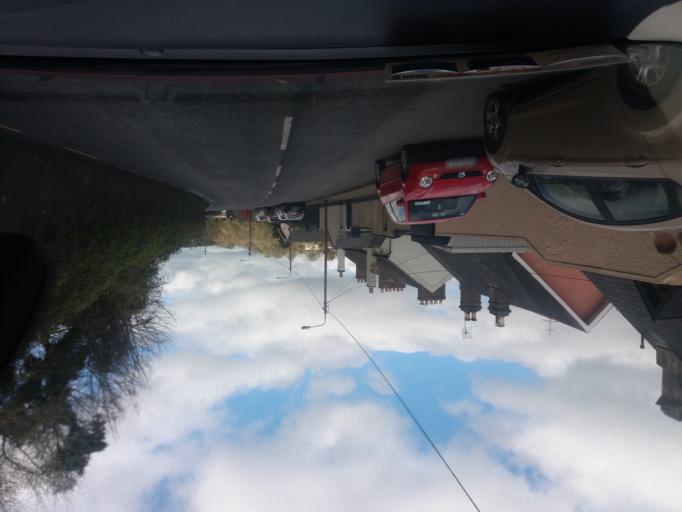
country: IE
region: Munster
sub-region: County Cork
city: Cobh
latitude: 51.8516
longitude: -8.3259
